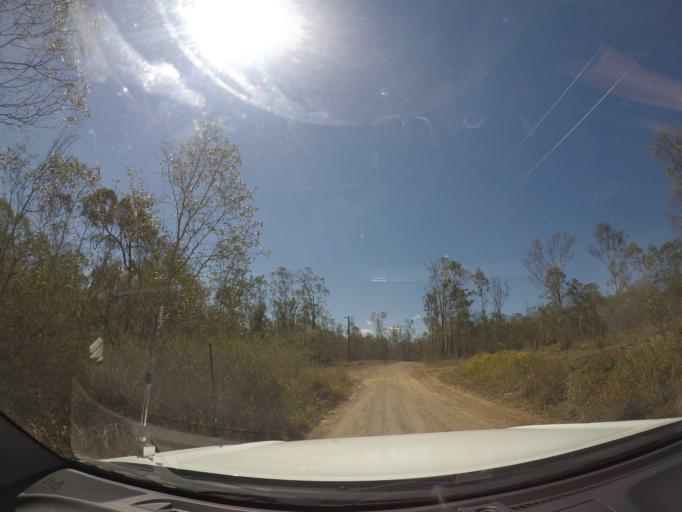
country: AU
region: Queensland
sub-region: Logan
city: North Maclean
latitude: -27.7714
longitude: 152.9372
